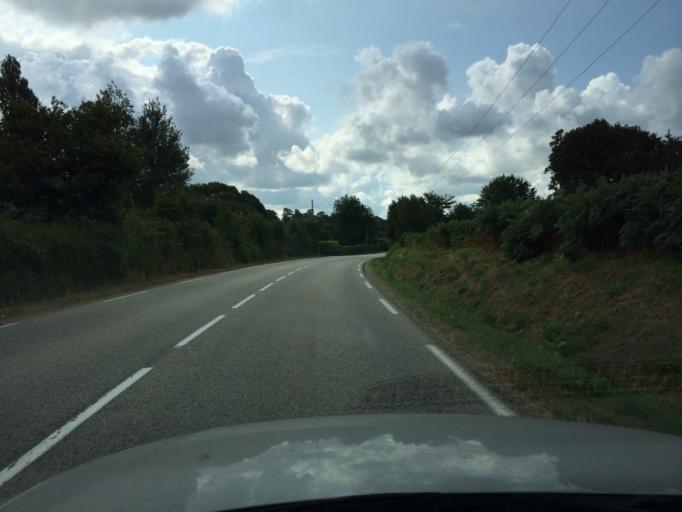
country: FR
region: Lower Normandy
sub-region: Departement de la Manche
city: Martinvast
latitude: 49.5666
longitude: -1.6926
